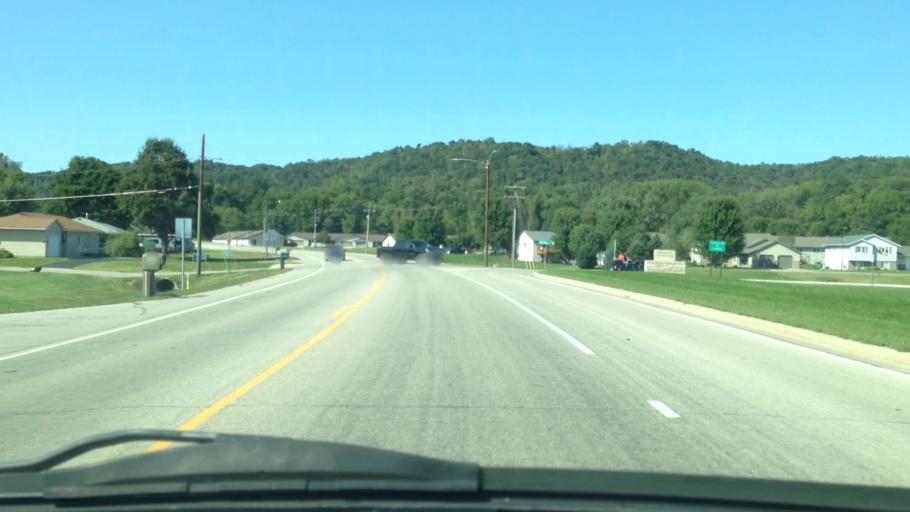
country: US
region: Minnesota
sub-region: Fillmore County
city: Rushford
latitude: 43.8171
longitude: -91.7533
